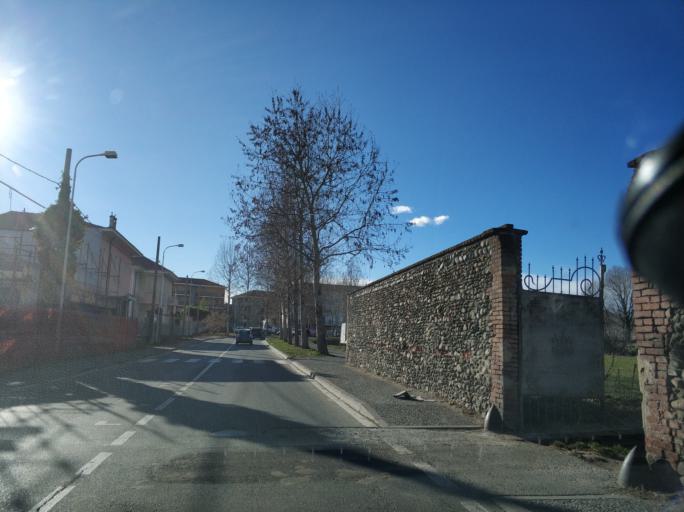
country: IT
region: Piedmont
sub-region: Provincia di Torino
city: Caselle Torinese
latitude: 45.1746
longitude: 7.6467
